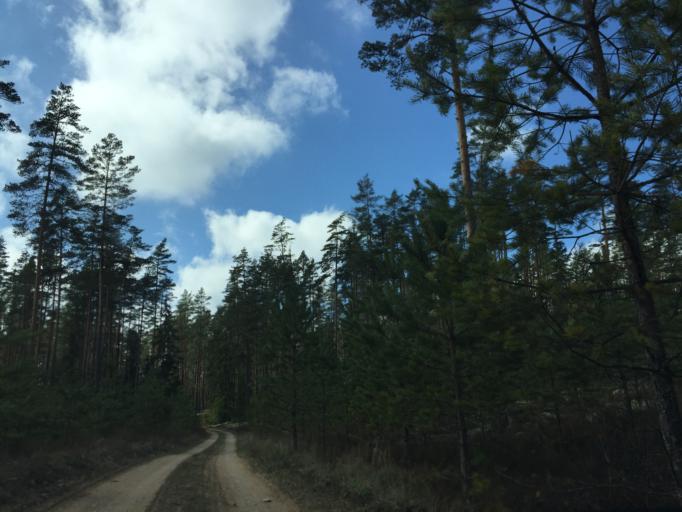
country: EE
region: Valgamaa
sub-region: Valga linn
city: Valga
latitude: 57.6205
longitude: 26.2080
